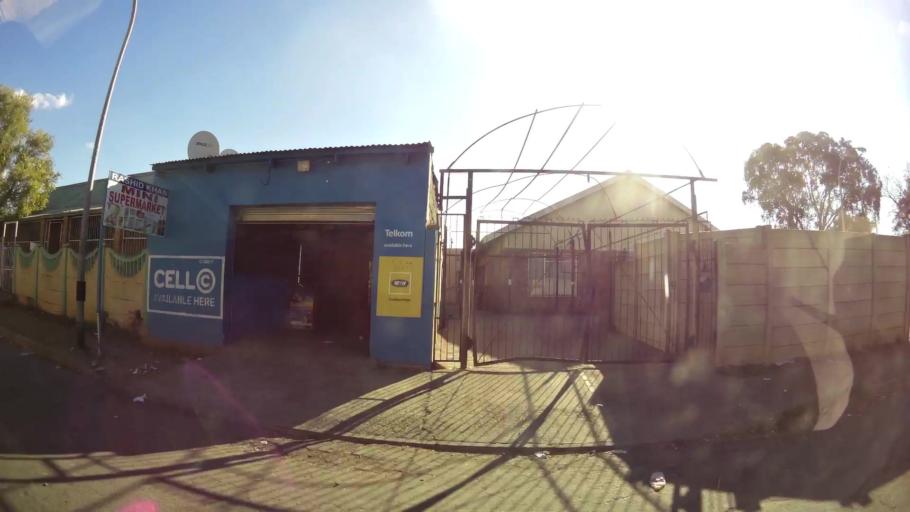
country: ZA
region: Northern Cape
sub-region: Frances Baard District Municipality
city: Kimberley
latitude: -28.7341
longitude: 24.7652
